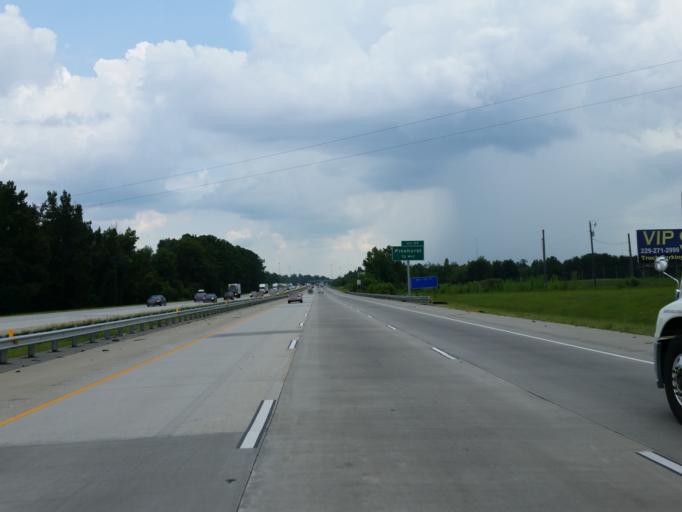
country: US
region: Georgia
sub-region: Dooly County
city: Unadilla
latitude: 32.2028
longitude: -83.7467
